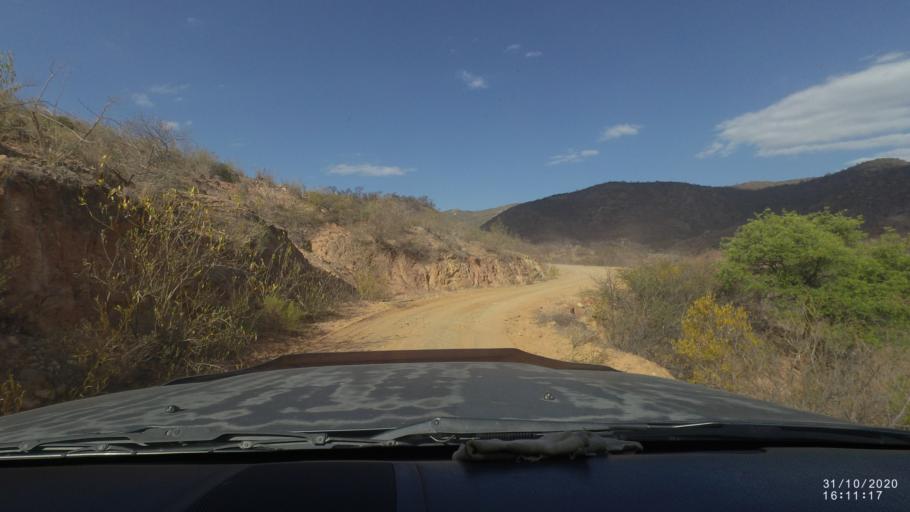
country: BO
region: Chuquisaca
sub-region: Provincia Zudanez
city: Mojocoya
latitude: -18.3805
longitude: -64.6249
